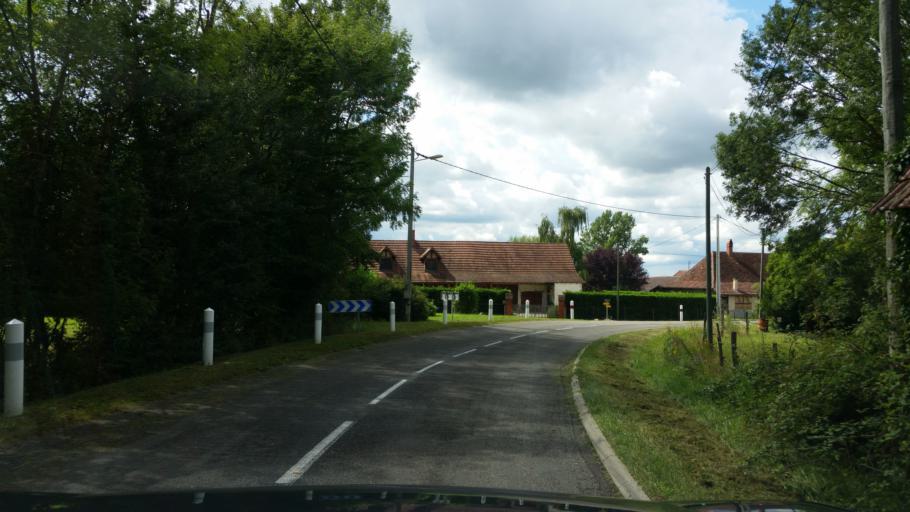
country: FR
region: Bourgogne
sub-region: Departement de Saone-et-Loire
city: Saint-Usuge
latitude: 46.7030
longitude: 5.3449
